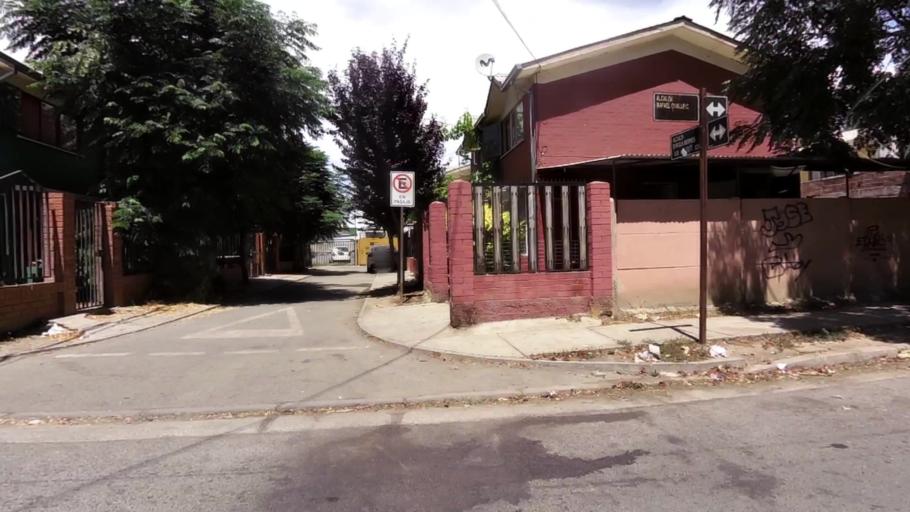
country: CL
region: O'Higgins
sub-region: Provincia de Cachapoal
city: Graneros
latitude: -34.0590
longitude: -70.7307
